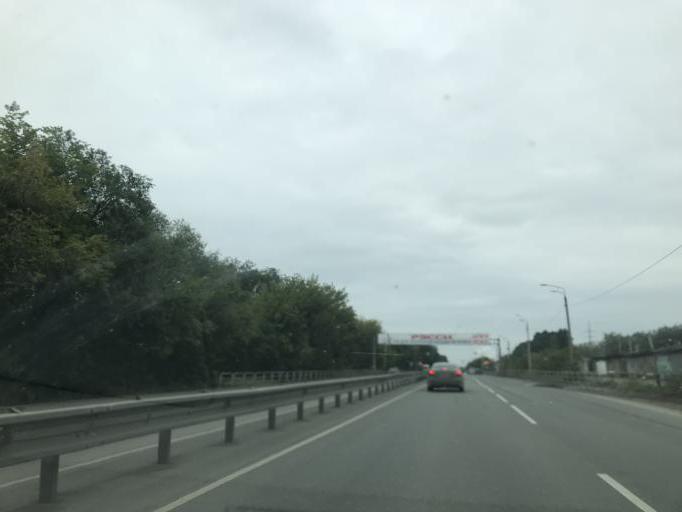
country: RU
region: Chelyabinsk
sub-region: Gorod Chelyabinsk
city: Chelyabinsk
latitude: 55.1777
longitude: 61.4213
